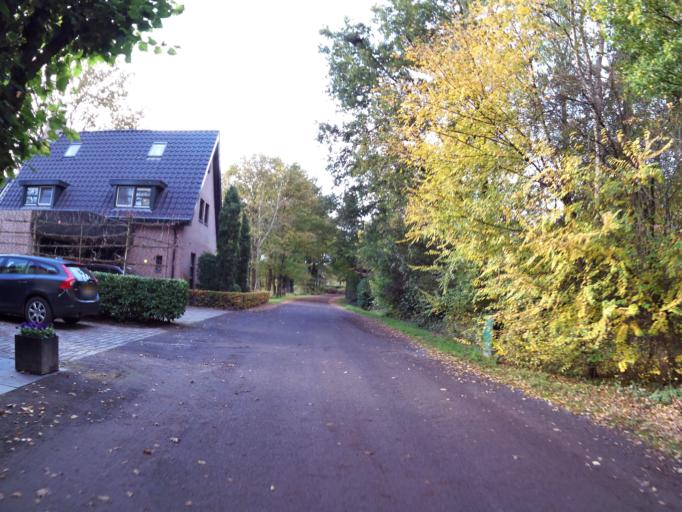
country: NL
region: North Brabant
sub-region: Gemeente Vught
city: Vught
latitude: 51.6556
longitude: 5.2377
